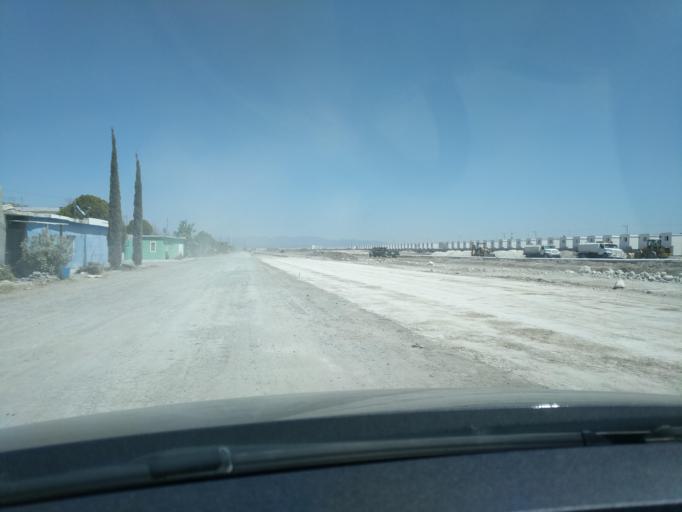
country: MX
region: Nuevo Leon
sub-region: Salinas Victoria
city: Emiliano Zapata
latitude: 25.9110
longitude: -100.2653
